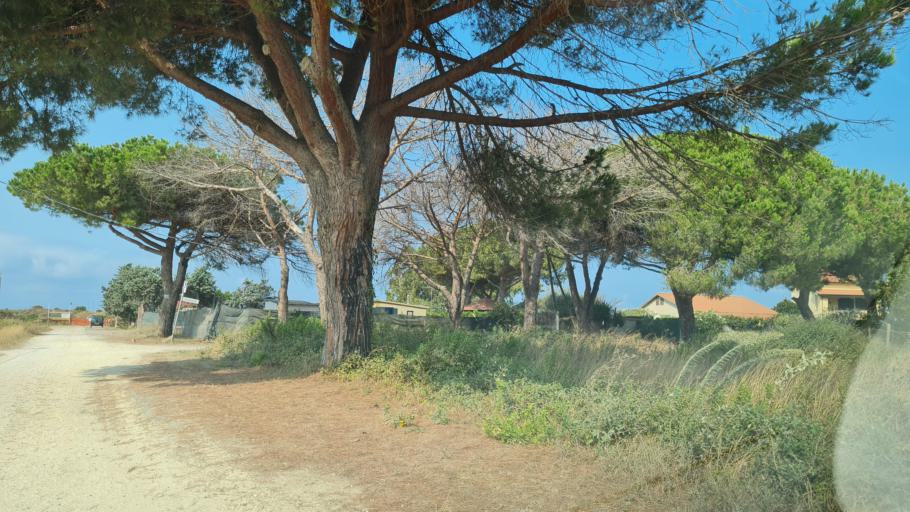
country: IT
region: Latium
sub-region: Provincia di Viterbo
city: Tarquinia
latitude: 42.1937
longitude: 11.7269
